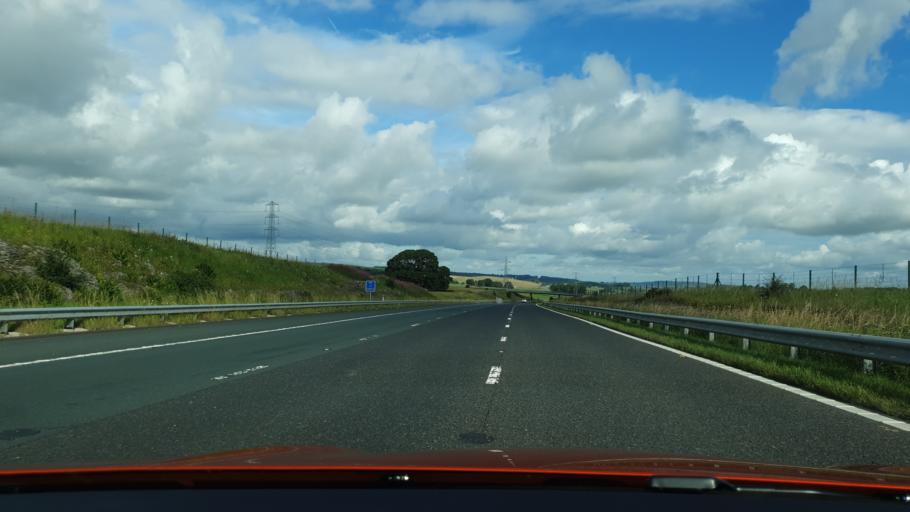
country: GB
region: England
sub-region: Cumbria
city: Penrith
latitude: 54.5433
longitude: -2.6662
